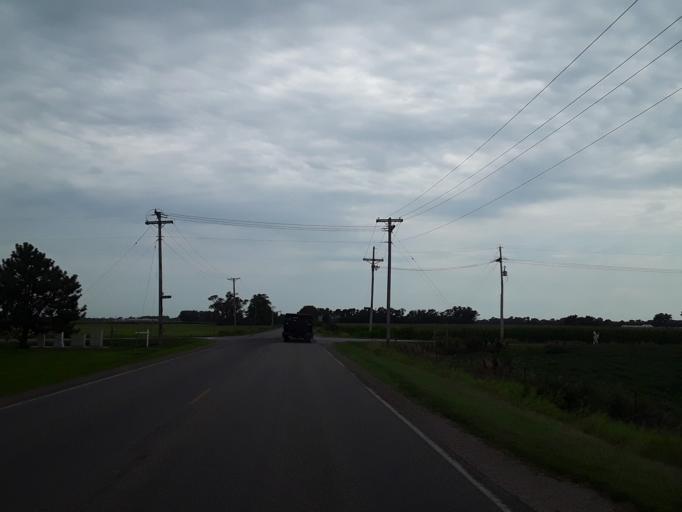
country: US
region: Nebraska
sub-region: Douglas County
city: Valley
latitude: 41.2490
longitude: -96.3305
